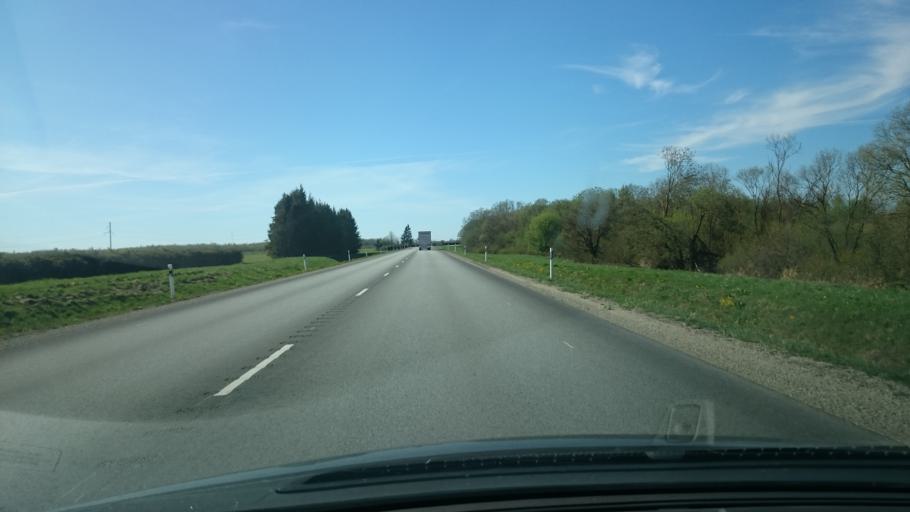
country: EE
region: Ida-Virumaa
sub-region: Kivioli linn
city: Kivioli
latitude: 59.4160
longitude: 26.9782
